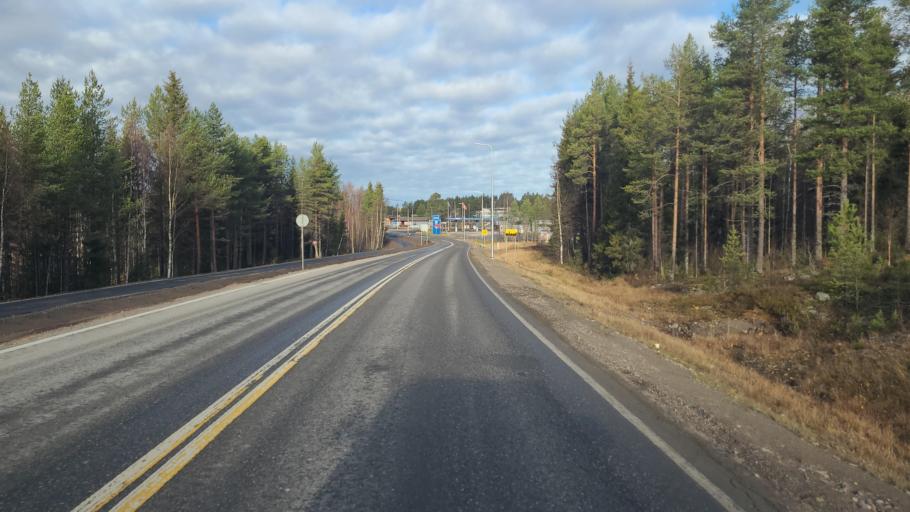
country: FI
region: Lapland
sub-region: Itae-Lappi
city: Posio
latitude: 66.1067
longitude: 28.1803
